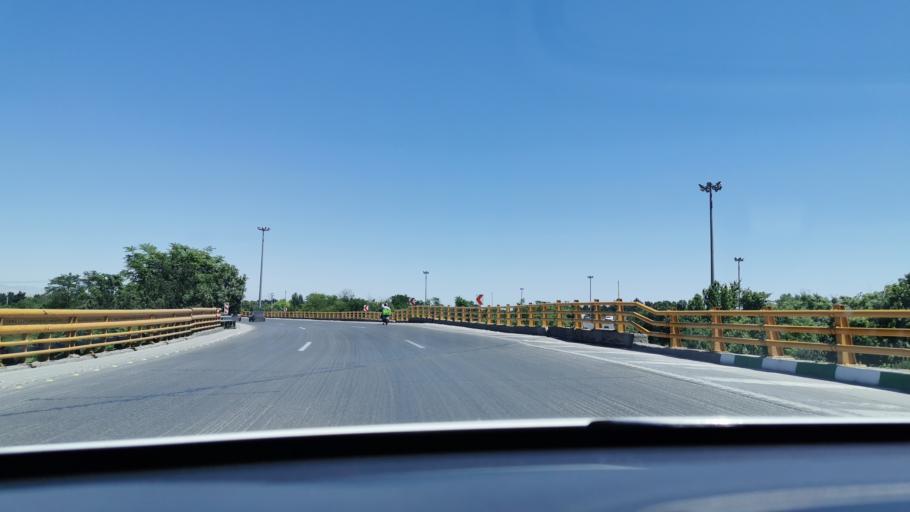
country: IR
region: Razavi Khorasan
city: Mashhad
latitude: 36.2496
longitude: 59.6090
